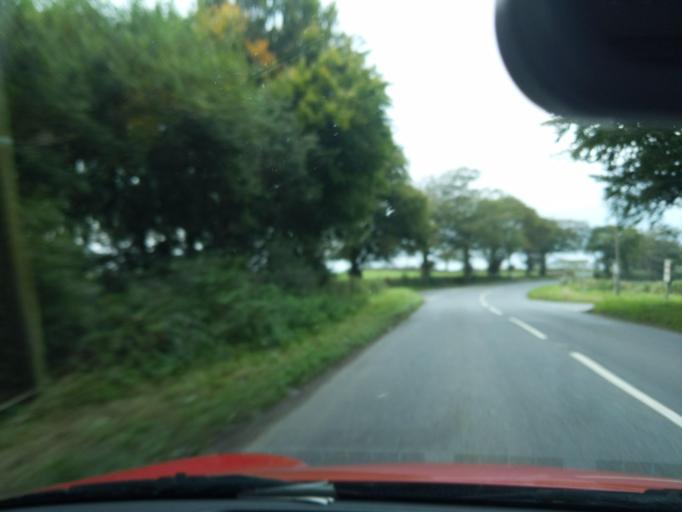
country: GB
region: England
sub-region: Devon
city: Okehampton
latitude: 50.7171
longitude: -4.0543
